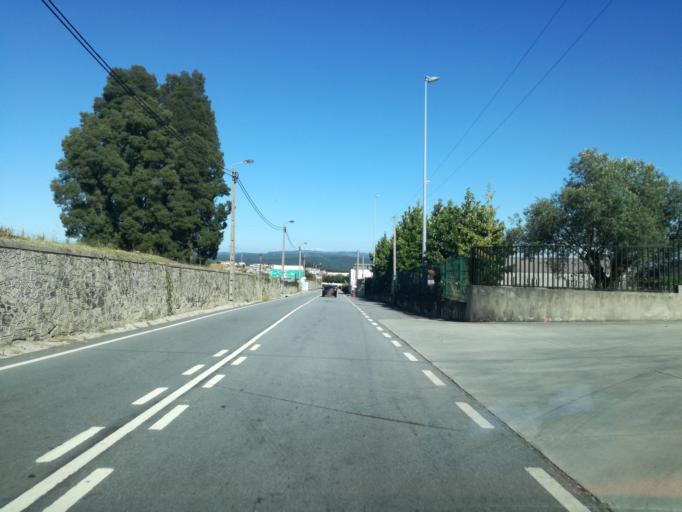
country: PT
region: Porto
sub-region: Trofa
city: Sao Romao do Coronado
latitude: 41.2829
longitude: -8.5831
